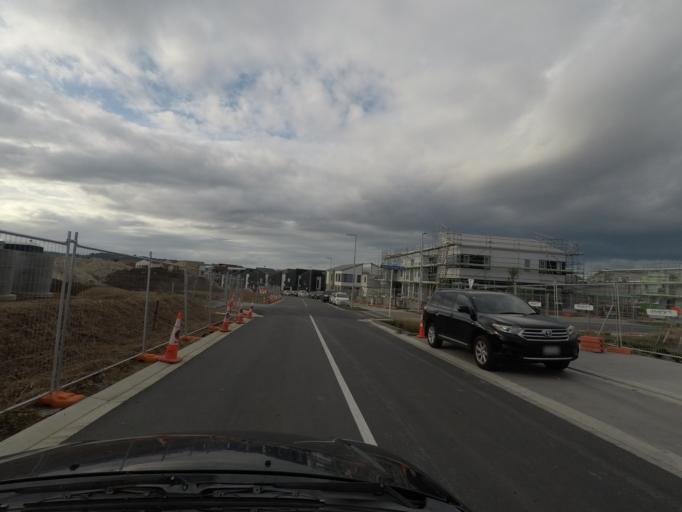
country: NZ
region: Auckland
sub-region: Auckland
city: Rosebank
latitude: -36.7985
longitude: 174.6534
